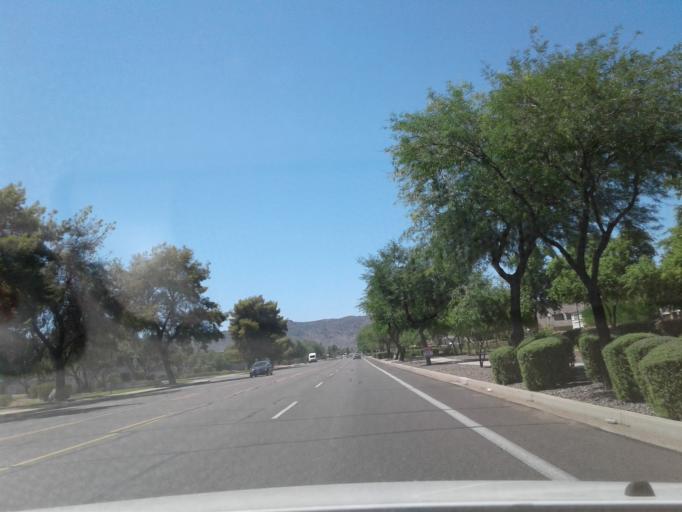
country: US
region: Arizona
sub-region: Maricopa County
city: Phoenix
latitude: 33.3987
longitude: -112.0301
